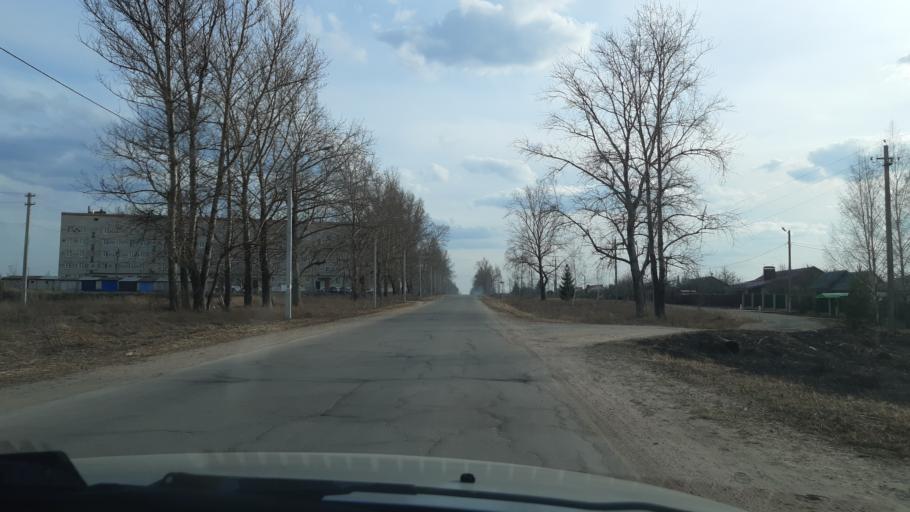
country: RU
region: Vladimir
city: Nikologory
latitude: 56.1336
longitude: 41.9910
